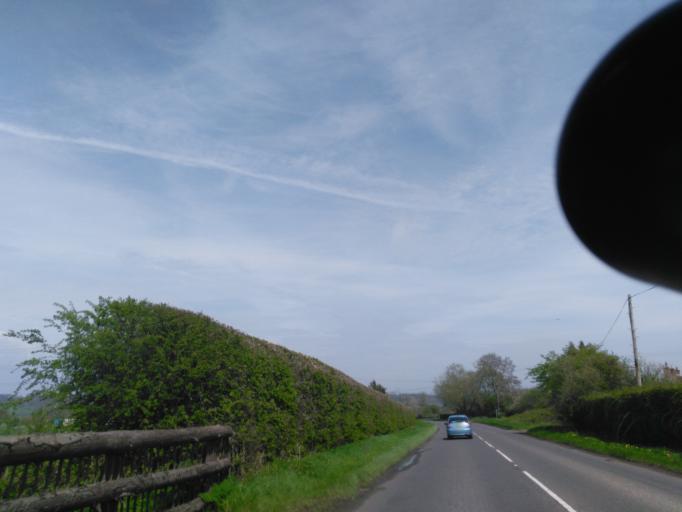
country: GB
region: England
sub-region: Somerset
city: Wells
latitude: 51.1559
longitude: -2.6131
